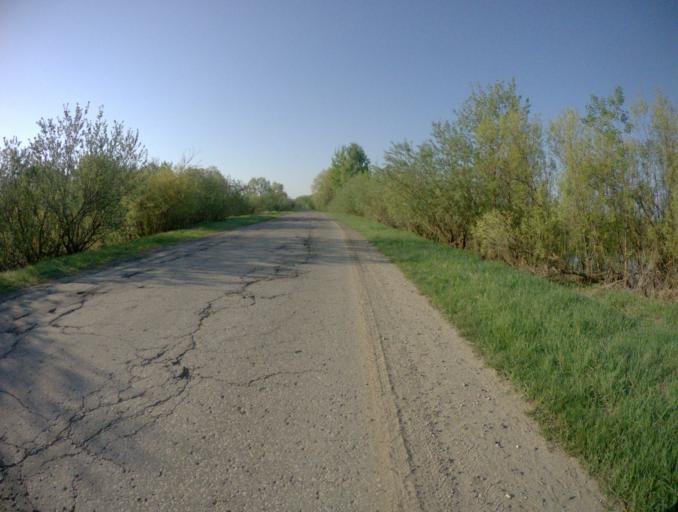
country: RU
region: Vladimir
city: Vyazniki
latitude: 56.2624
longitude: 42.1710
